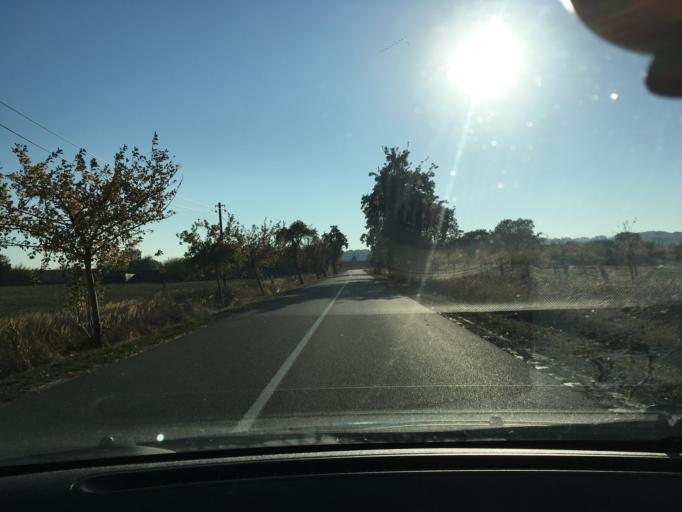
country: DE
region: Lower Saxony
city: Hitzacker
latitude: 53.1637
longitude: 11.0561
